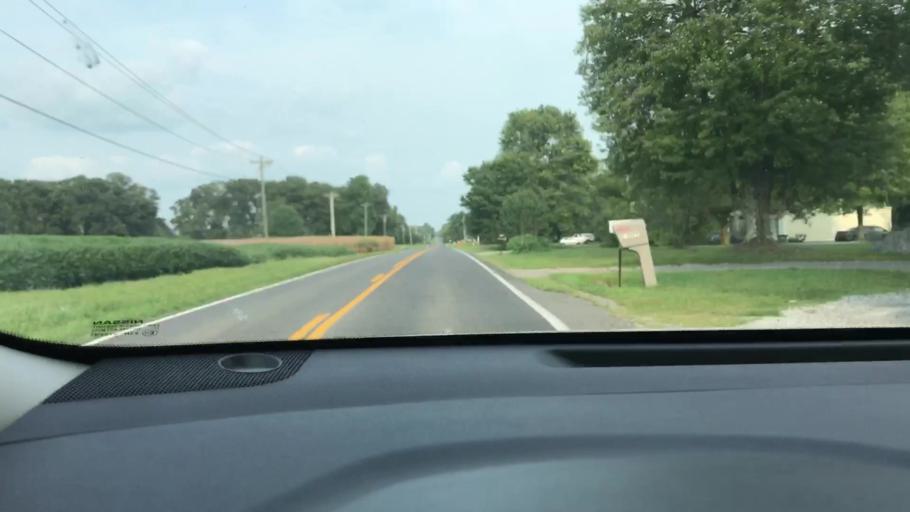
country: US
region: Kentucky
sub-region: Calloway County
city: Murray
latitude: 36.5806
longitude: -88.2623
